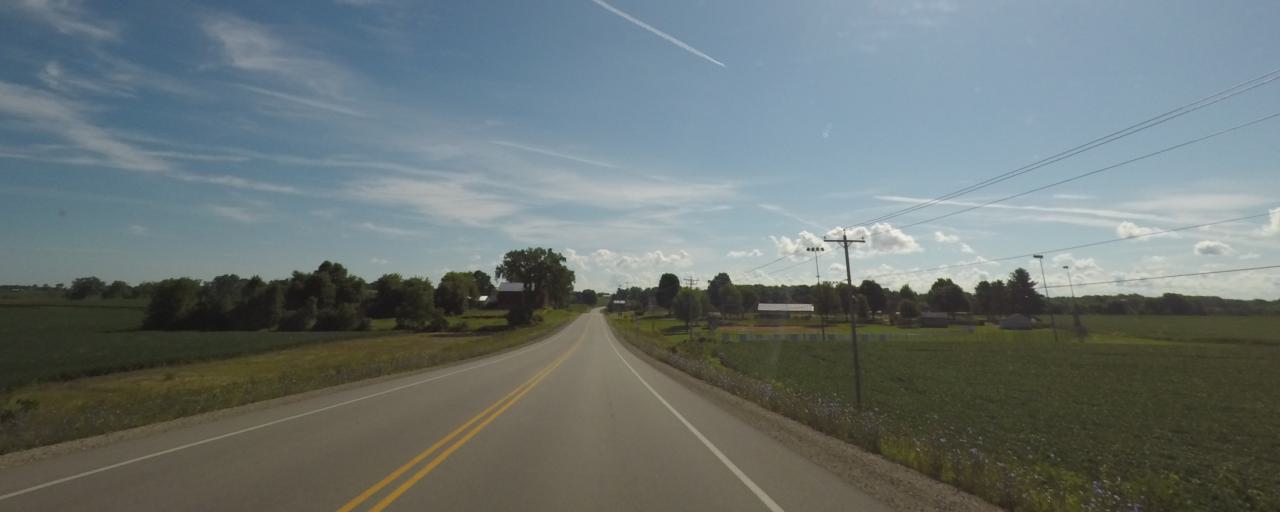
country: US
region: Wisconsin
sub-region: Jefferson County
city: Johnson Creek
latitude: 43.0726
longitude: -88.6867
